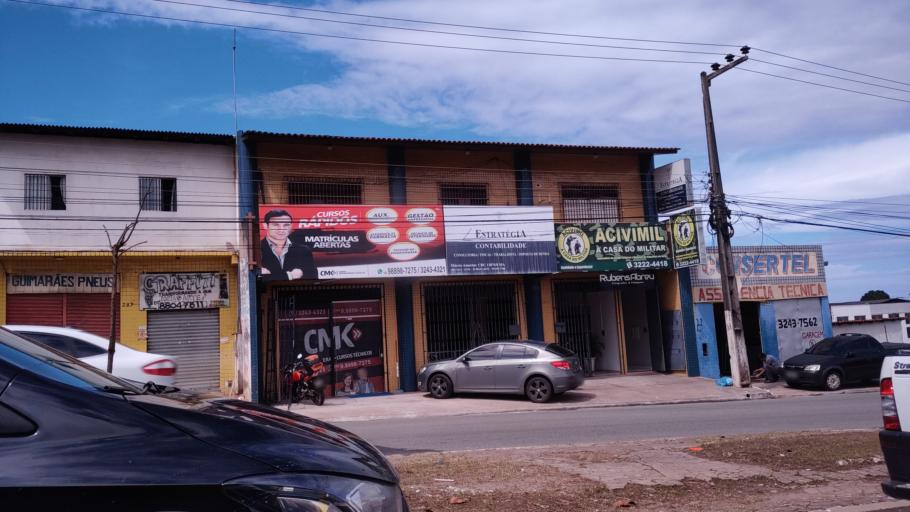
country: BR
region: Maranhao
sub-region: Sao Luis
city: Sao Luis
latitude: -2.5391
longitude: -44.2673
